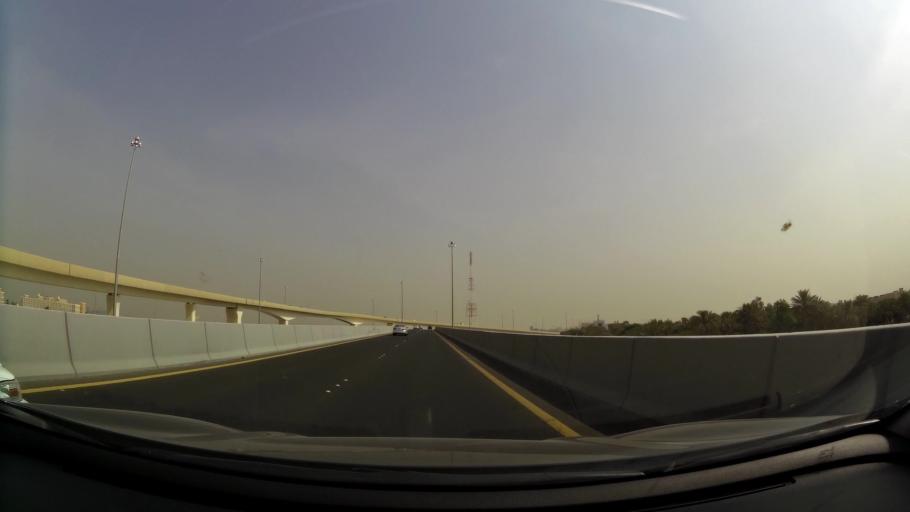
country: KW
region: Al Asimah
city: Ar Rabiyah
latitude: 29.3096
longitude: 47.8834
